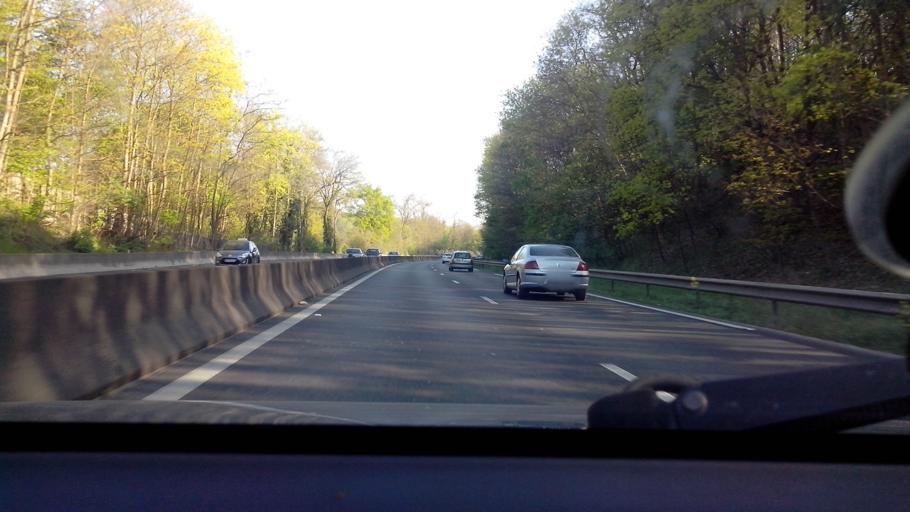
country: FR
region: Ile-de-France
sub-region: Departement de l'Essonne
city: Bievres
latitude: 48.7565
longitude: 2.2238
